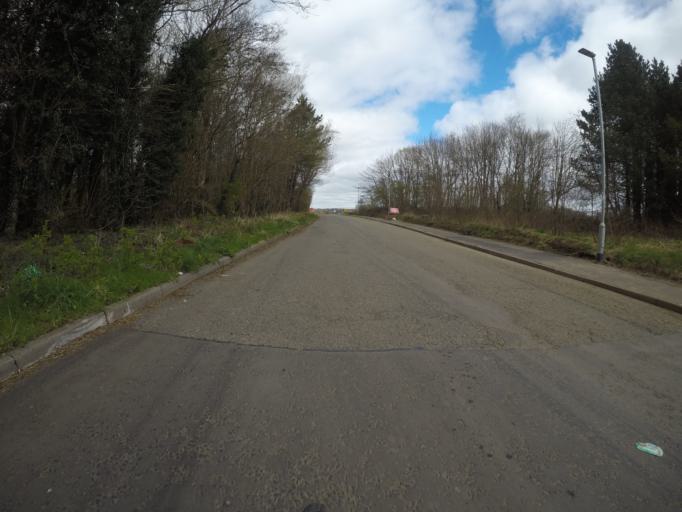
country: GB
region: Scotland
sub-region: North Ayrshire
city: Irvine
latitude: 55.6176
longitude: -4.6450
